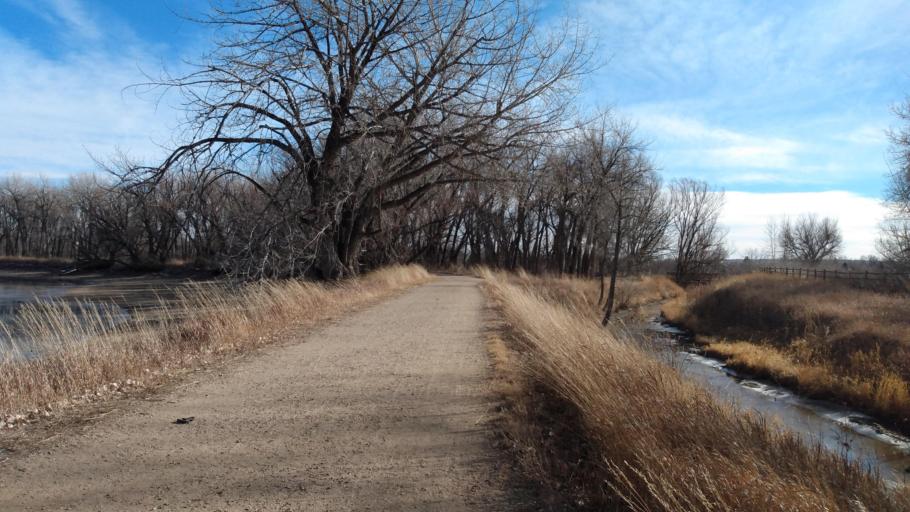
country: US
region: Colorado
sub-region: Boulder County
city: Gunbarrel
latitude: 40.0617
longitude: -105.1994
